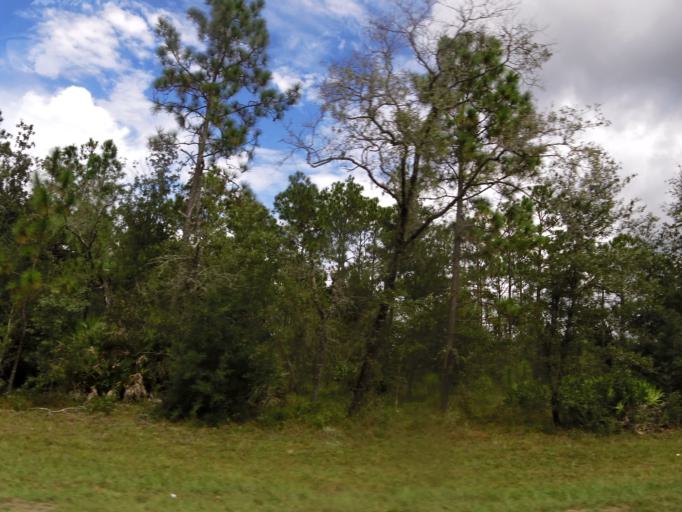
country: US
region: Florida
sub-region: Clay County
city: Middleburg
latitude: 30.1086
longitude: -81.9624
